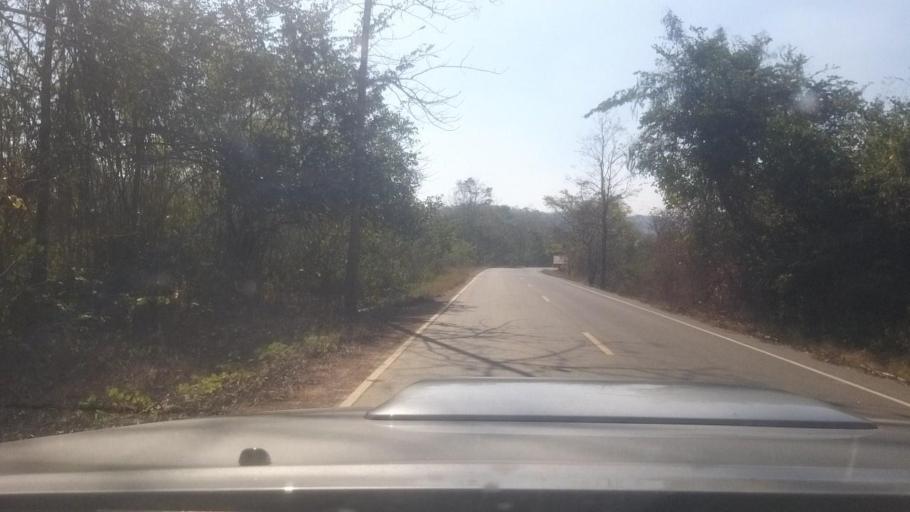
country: TH
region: Phrae
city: Nong Muang Khai
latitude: 18.2966
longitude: 100.0441
